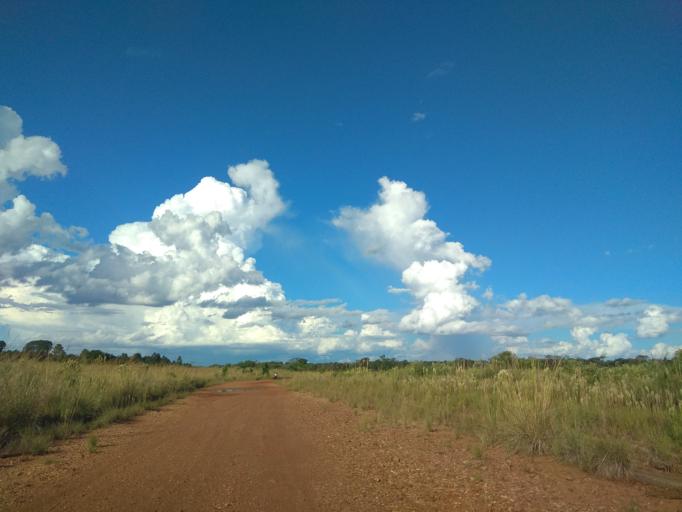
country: AR
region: Misiones
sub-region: Departamento de Candelaria
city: Candelaria
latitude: -27.4957
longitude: -55.7675
